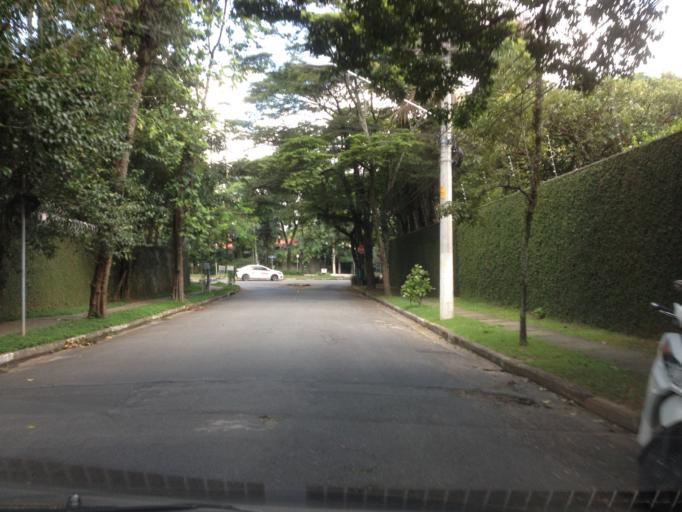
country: BR
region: Sao Paulo
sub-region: Sao Paulo
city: Sao Paulo
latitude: -23.5450
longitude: -46.7136
